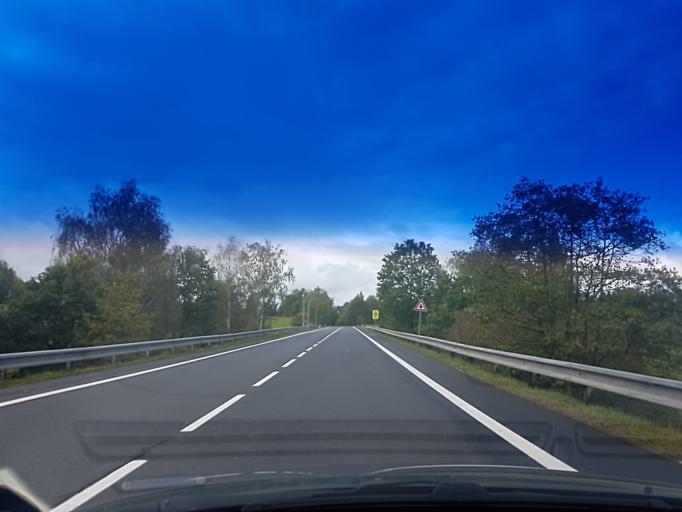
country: CZ
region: Karlovarsky
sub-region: Okres Cheb
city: Frantiskovy Lazne
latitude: 50.0831
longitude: 12.3055
